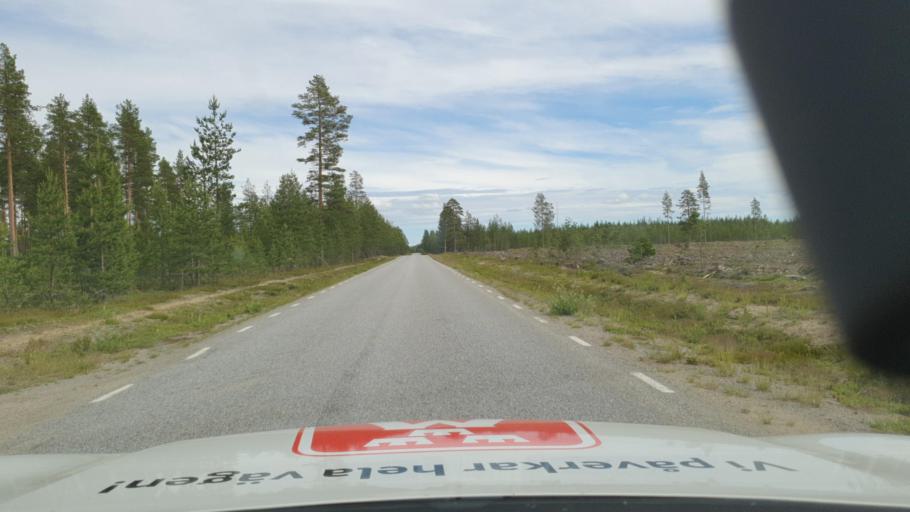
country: SE
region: Vaesterbotten
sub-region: Skelleftea Kommun
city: Burtraesk
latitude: 64.5050
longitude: 20.8070
